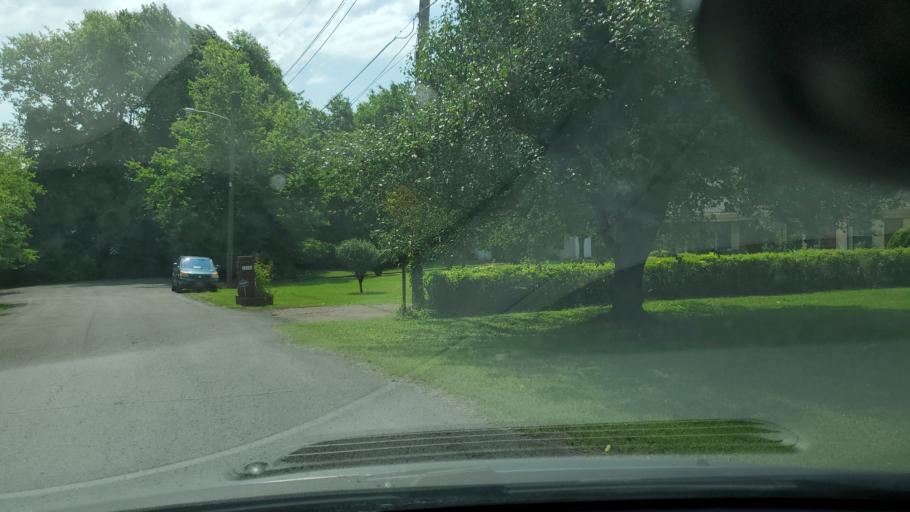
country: US
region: Tennessee
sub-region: Davidson County
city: Lakewood
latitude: 36.2273
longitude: -86.7177
